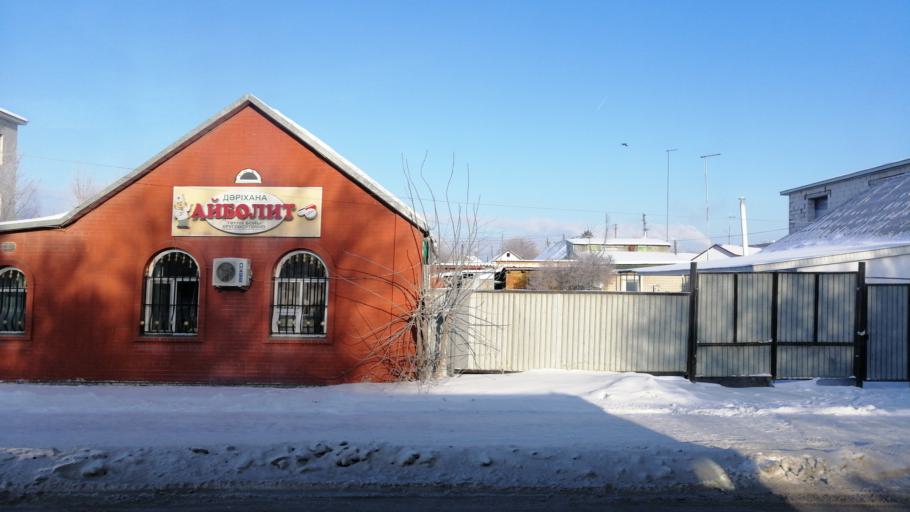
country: KZ
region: Aqtoebe
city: Aqtobe
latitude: 50.2998
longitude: 57.1486
